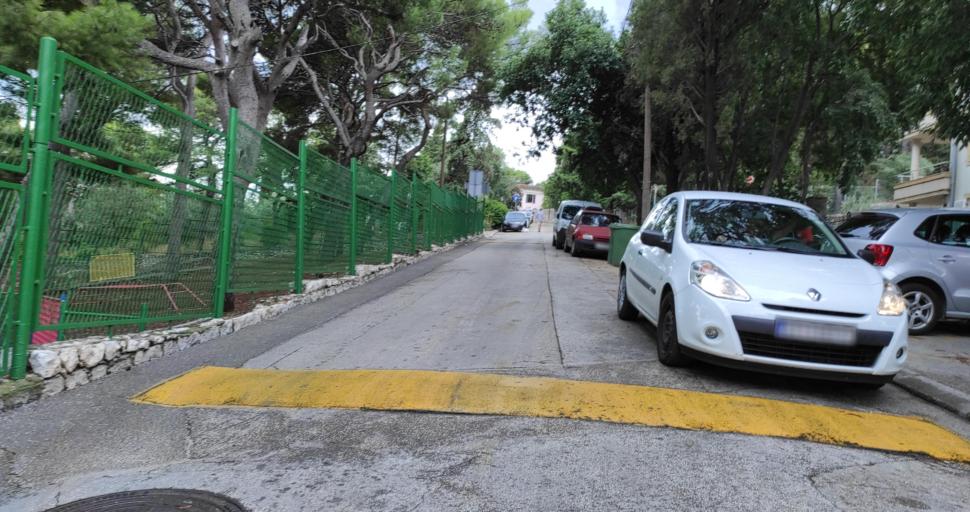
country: HR
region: Splitsko-Dalmatinska
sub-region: Grad Split
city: Split
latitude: 43.5091
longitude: 16.4307
